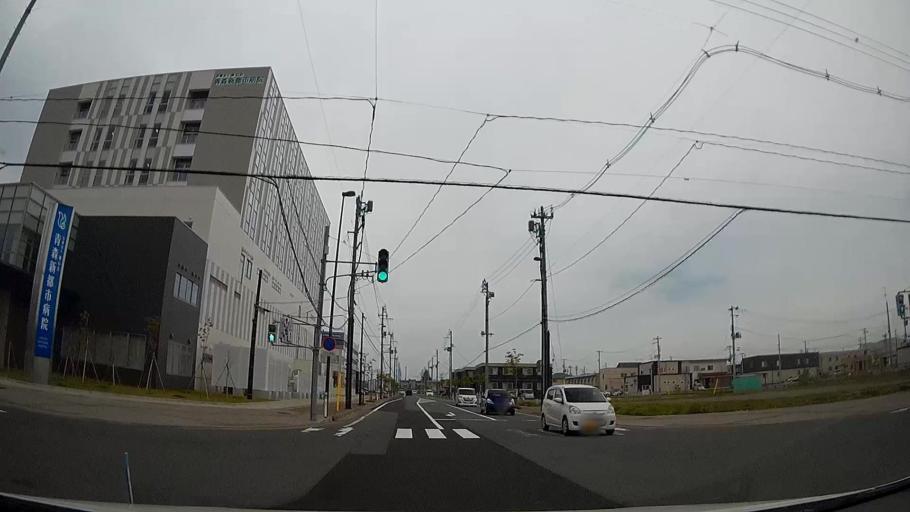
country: JP
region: Aomori
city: Aomori Shi
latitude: 40.8307
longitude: 140.6921
